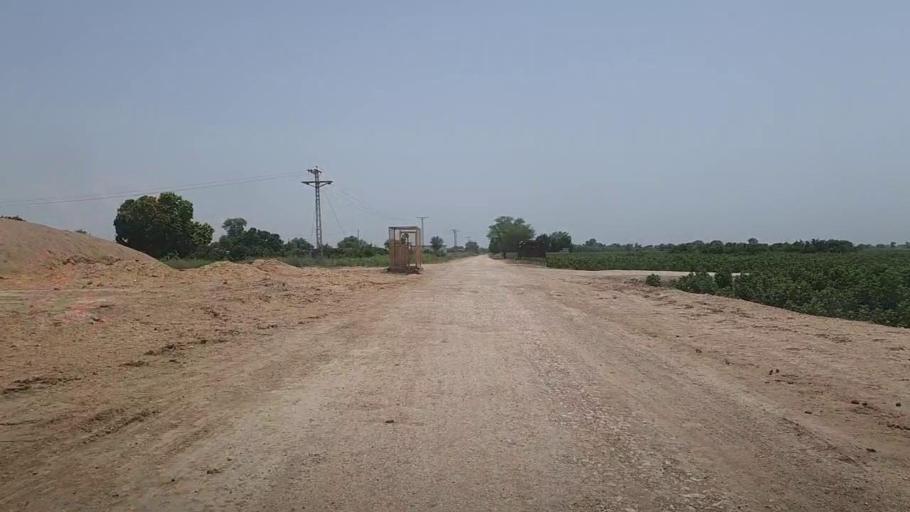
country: PK
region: Sindh
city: Pad Idan
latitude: 26.8420
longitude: 68.3247
